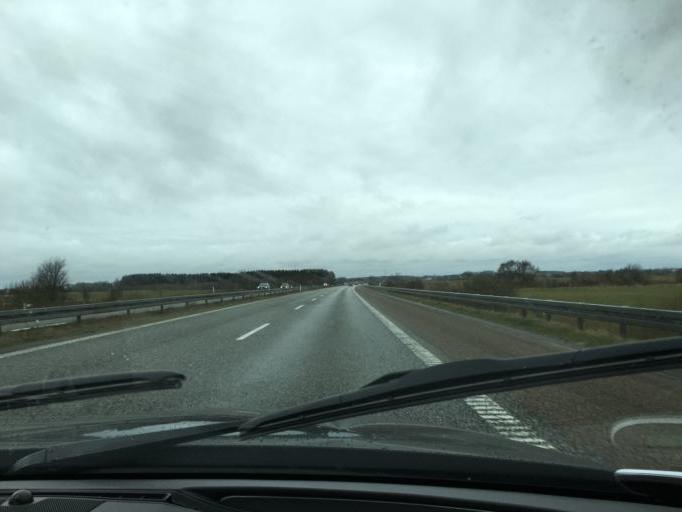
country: DK
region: South Denmark
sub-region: Esbjerg Kommune
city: Bramming
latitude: 55.5079
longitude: 8.6563
